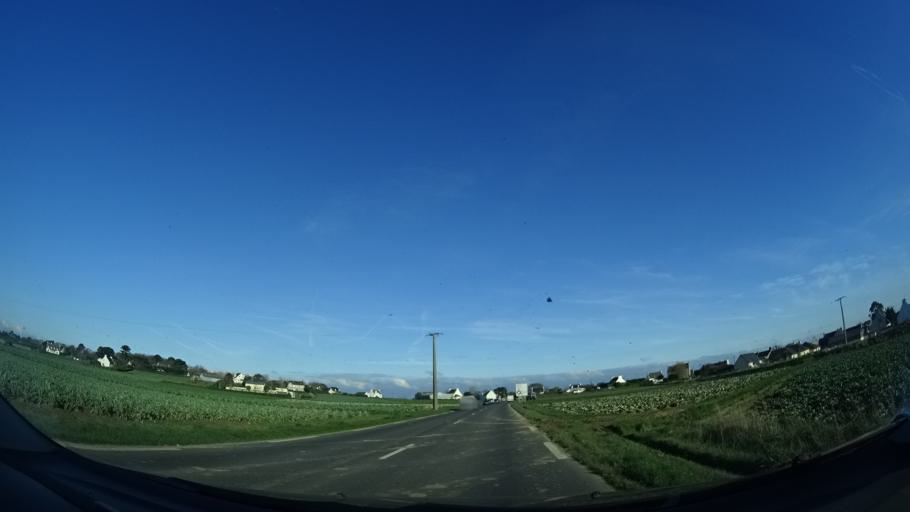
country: FR
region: Brittany
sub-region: Departement du Finistere
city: Saint-Pol-de-Leon
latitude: 48.7010
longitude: -3.9908
